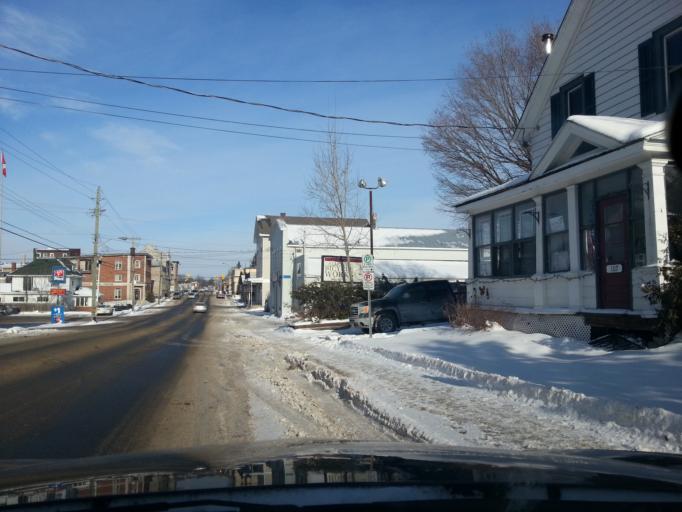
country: CA
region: Ontario
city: Carleton Place
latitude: 45.2236
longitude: -76.1948
